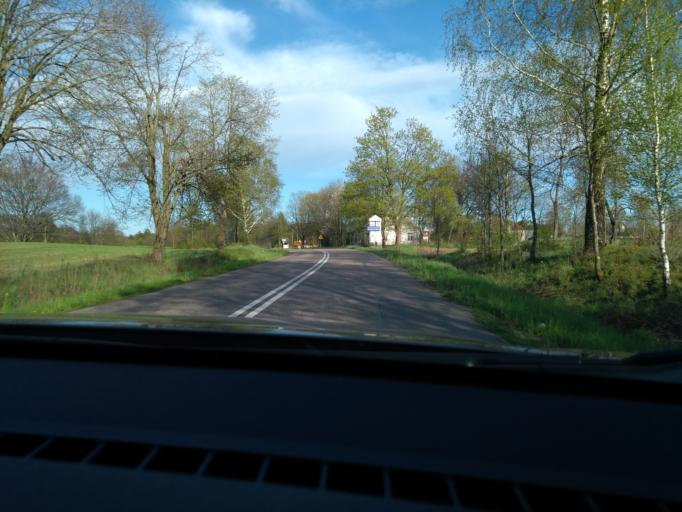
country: PL
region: Pomeranian Voivodeship
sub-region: Powiat leborski
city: Cewice
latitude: 54.3392
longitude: 17.7456
